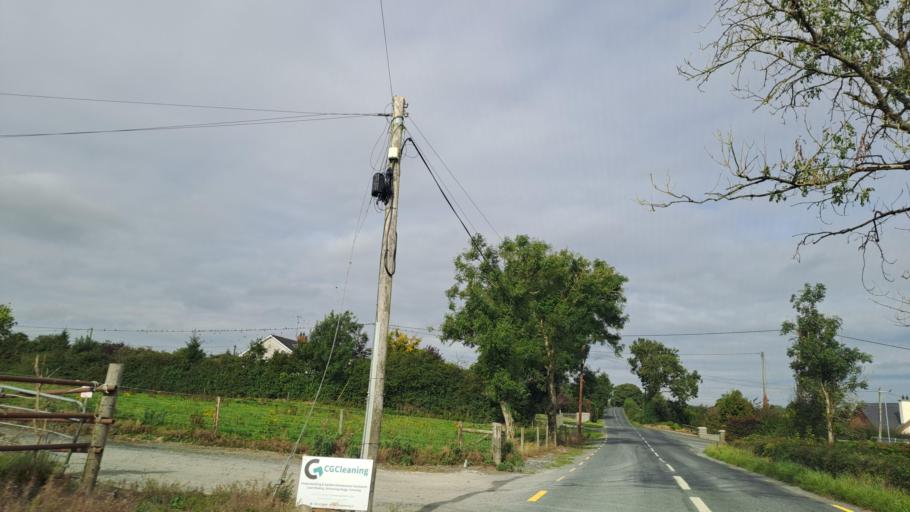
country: IE
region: Ulster
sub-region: An Cabhan
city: Kingscourt
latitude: 53.9811
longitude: -6.8801
